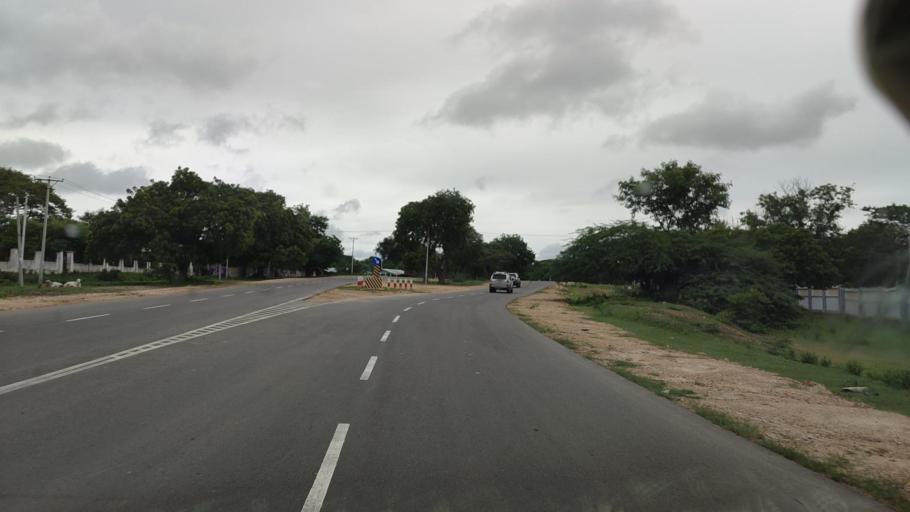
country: MM
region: Mandalay
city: Meiktila
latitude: 20.8585
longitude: 95.8711
